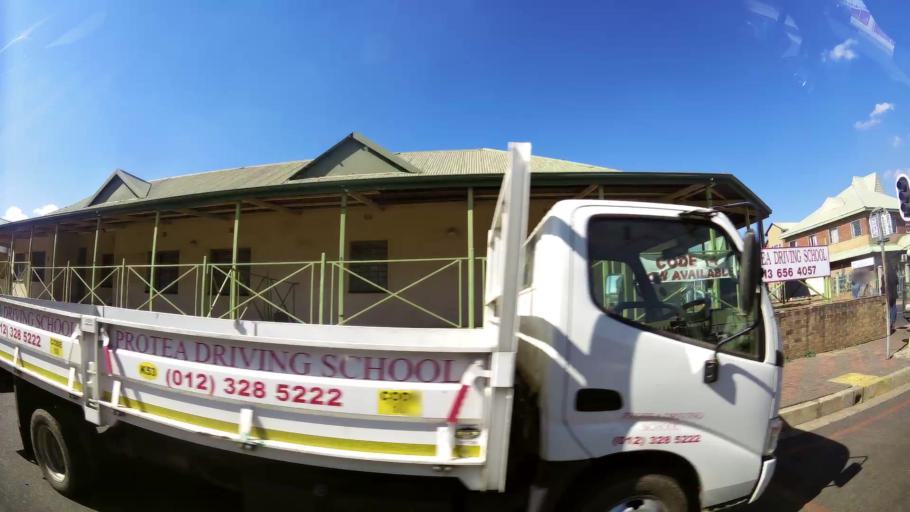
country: ZA
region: Mpumalanga
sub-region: Nkangala District Municipality
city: Witbank
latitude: -25.8759
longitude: 29.2165
